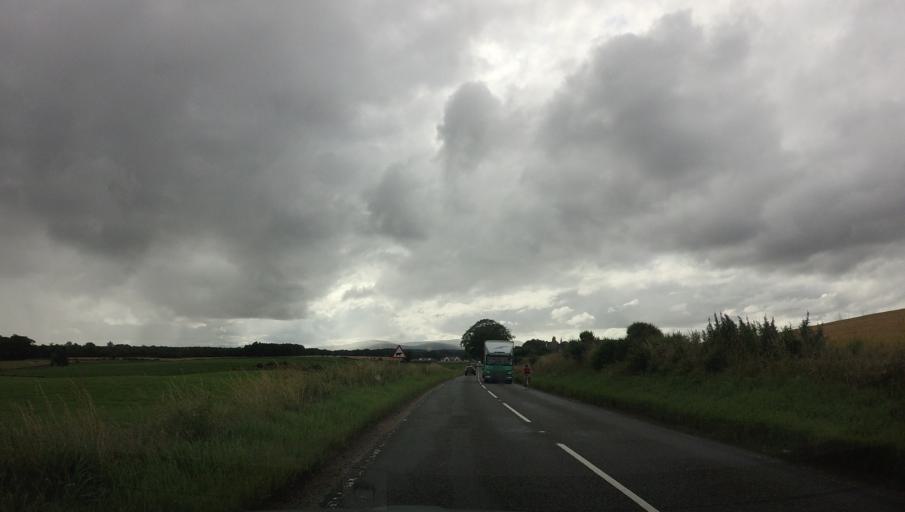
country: GB
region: Scotland
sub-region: Aberdeenshire
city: Westhill
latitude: 57.1420
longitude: -2.3154
